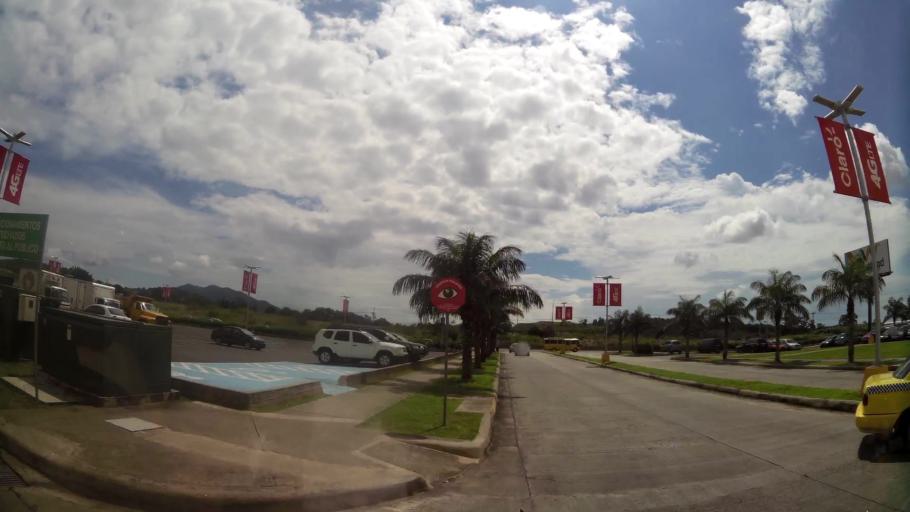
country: PA
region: Panama
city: Vista Alegre
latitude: 8.9225
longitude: -79.7030
